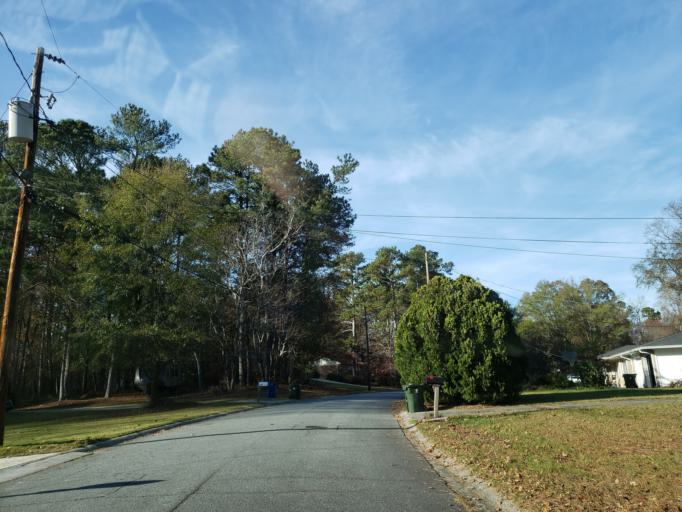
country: US
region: Georgia
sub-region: Cobb County
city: Kennesaw
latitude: 34.0237
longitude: -84.6068
